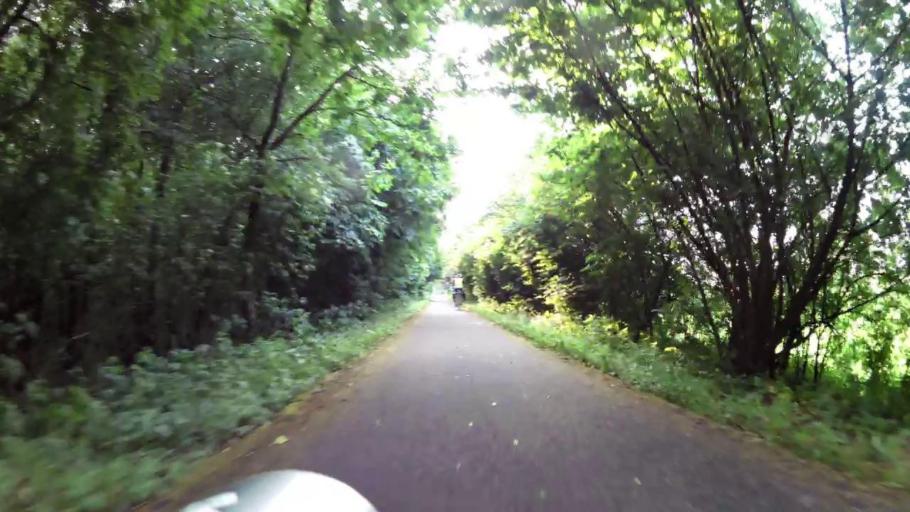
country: PL
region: Kujawsko-Pomorskie
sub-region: Powiat chelminski
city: Unislaw
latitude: 53.1842
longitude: 18.3880
